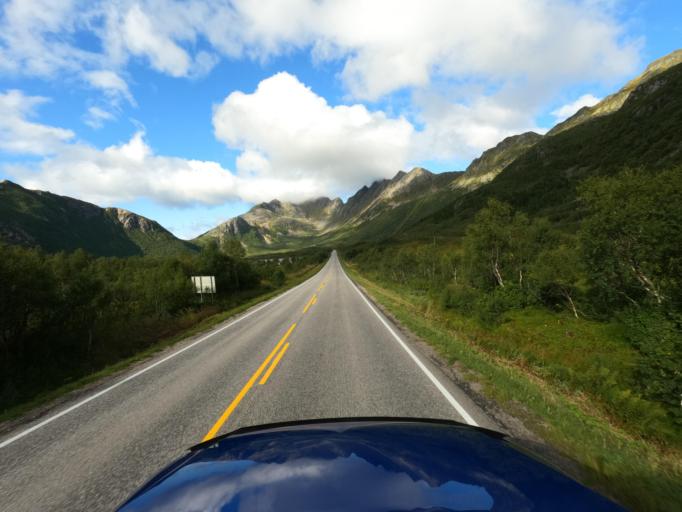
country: NO
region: Nordland
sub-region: Vagan
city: Kabelvag
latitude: 68.2119
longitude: 14.3475
